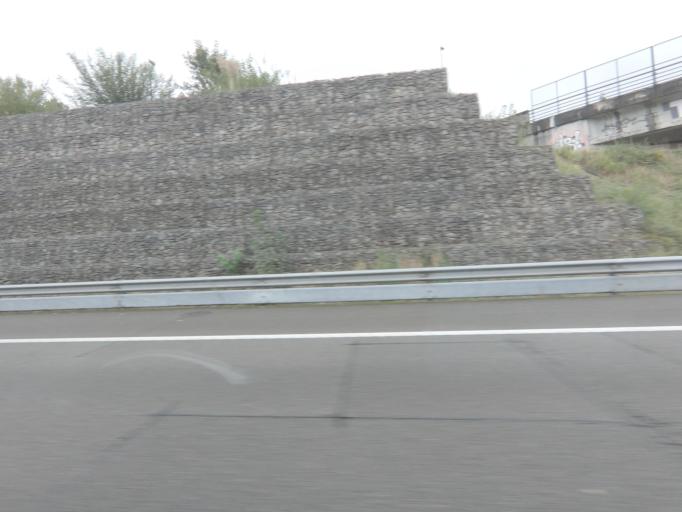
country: PT
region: Porto
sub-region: Matosinhos
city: Sao Mamede de Infesta
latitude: 41.2011
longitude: -8.6132
